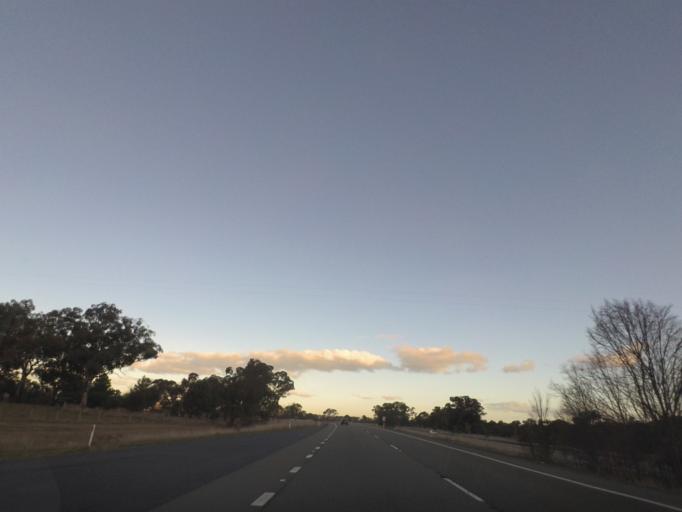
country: AU
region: New South Wales
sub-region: Yass Valley
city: Yass
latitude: -34.7797
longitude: 148.8423
